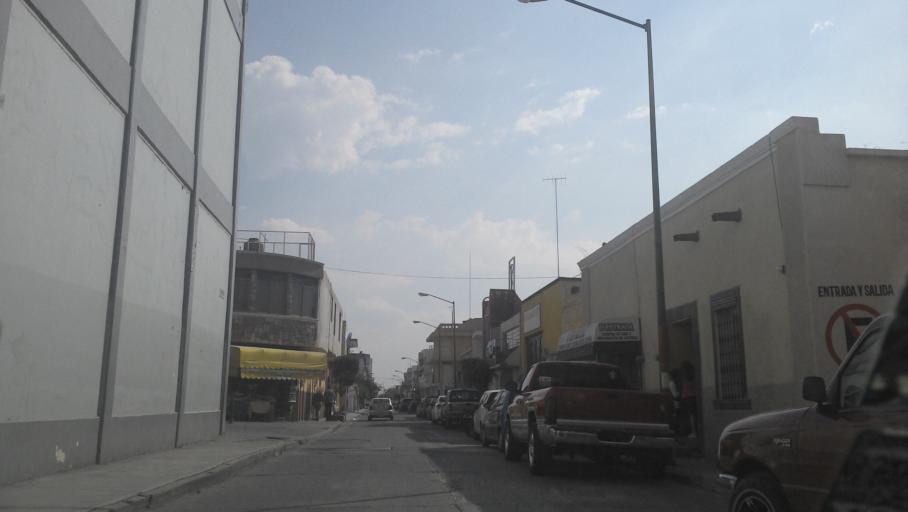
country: MX
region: Guanajuato
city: San Francisco del Rincon
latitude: 21.0180
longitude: -101.8596
